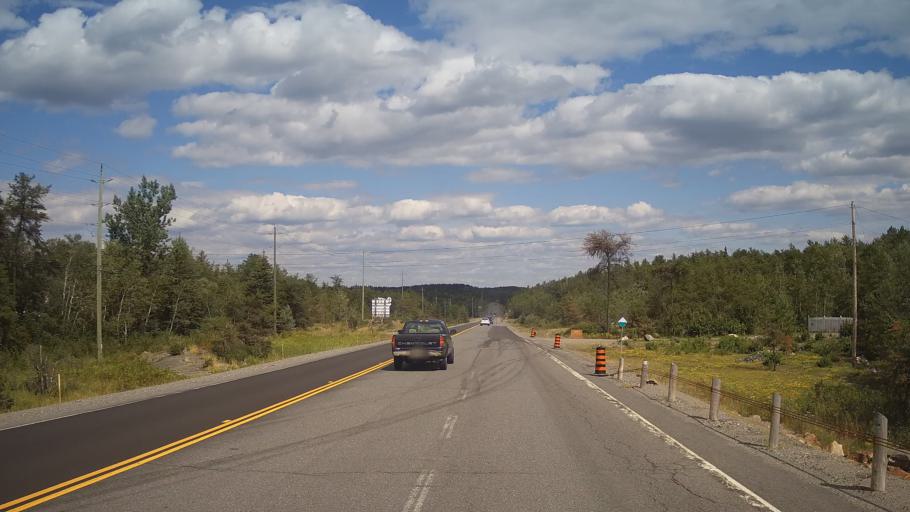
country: CA
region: Ontario
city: Greater Sudbury
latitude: 46.5210
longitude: -80.6740
